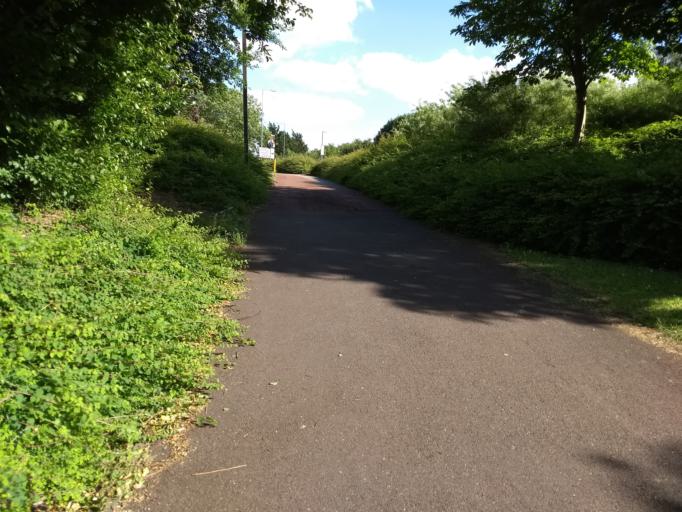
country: GB
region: England
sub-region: Milton Keynes
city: Shenley Church End
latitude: 52.0285
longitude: -0.7901
